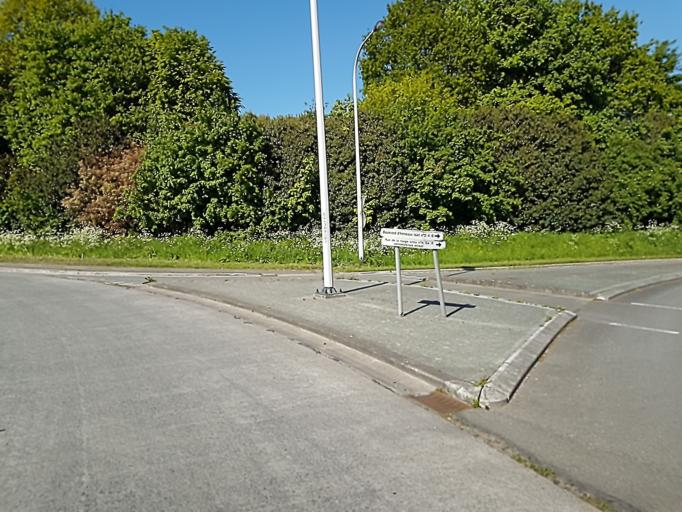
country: BE
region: Wallonia
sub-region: Province du Hainaut
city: Estaimpuis
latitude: 50.7240
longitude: 3.2932
